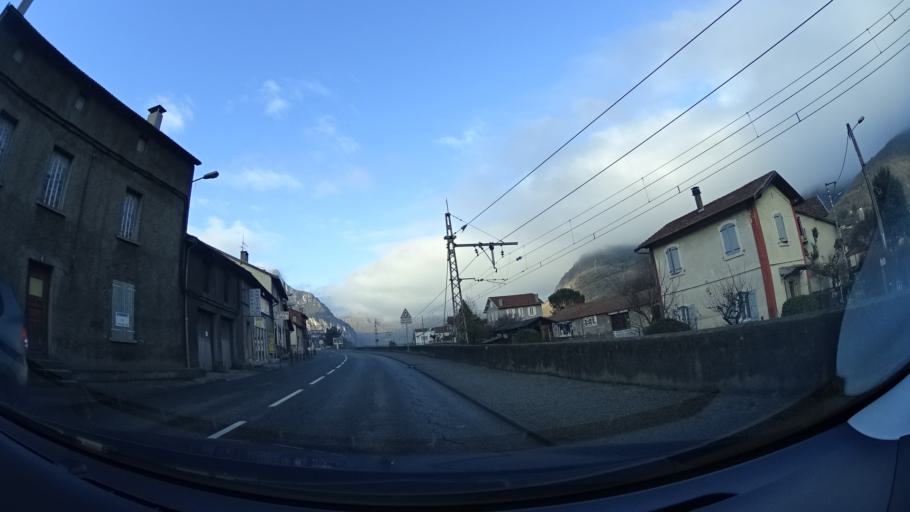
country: FR
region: Midi-Pyrenees
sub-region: Departement de l'Ariege
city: Tarascon-sur-Ariege
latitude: 42.8439
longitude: 1.6019
